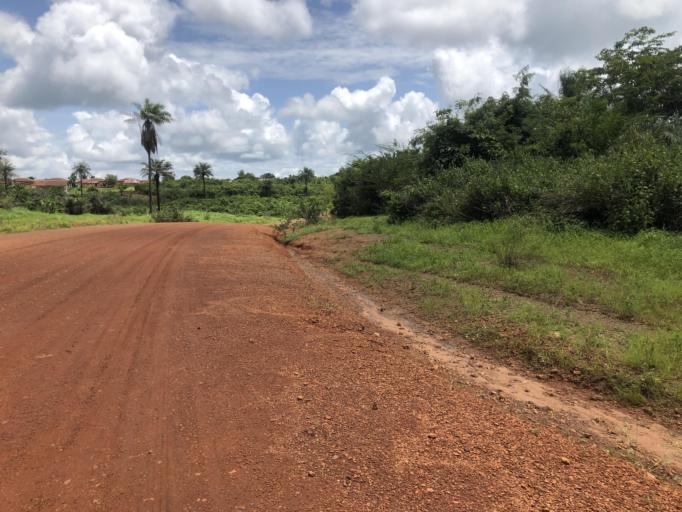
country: SL
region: Northern Province
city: Port Loko
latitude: 8.7167
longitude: -12.8452
